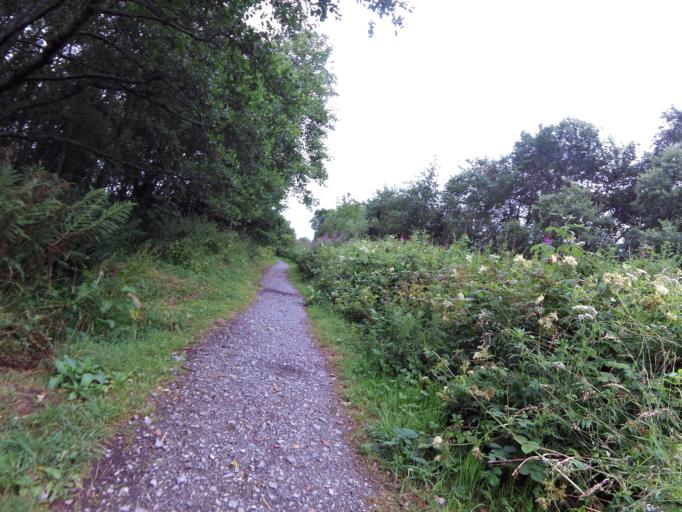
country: GB
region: Scotland
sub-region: Highland
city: Fort William
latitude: 56.8265
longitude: -5.0979
